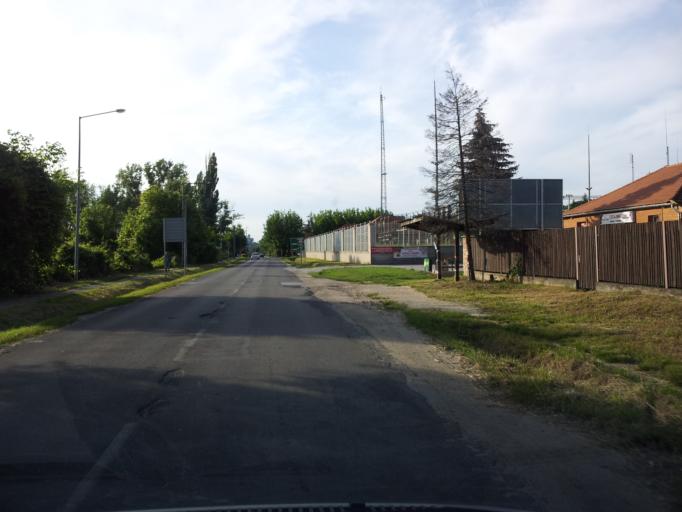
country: HU
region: Komarom-Esztergom
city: Esztergom
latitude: 47.7773
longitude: 18.7529
